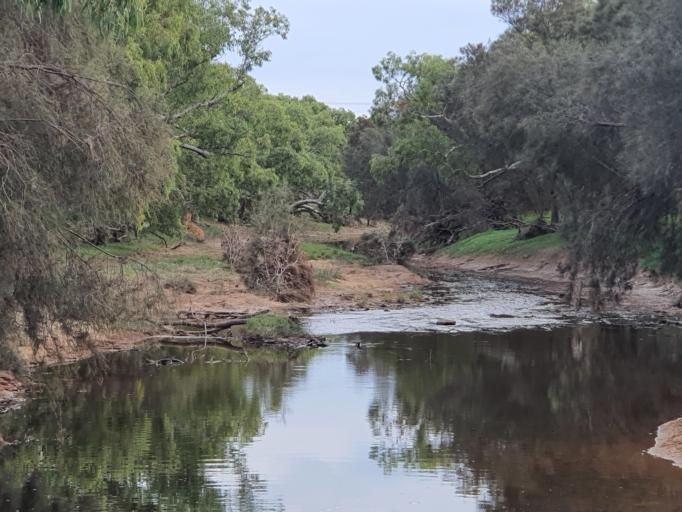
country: AU
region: Western Australia
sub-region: Geraldton-Greenough
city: Geraldton
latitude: -28.9058
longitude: 114.8076
